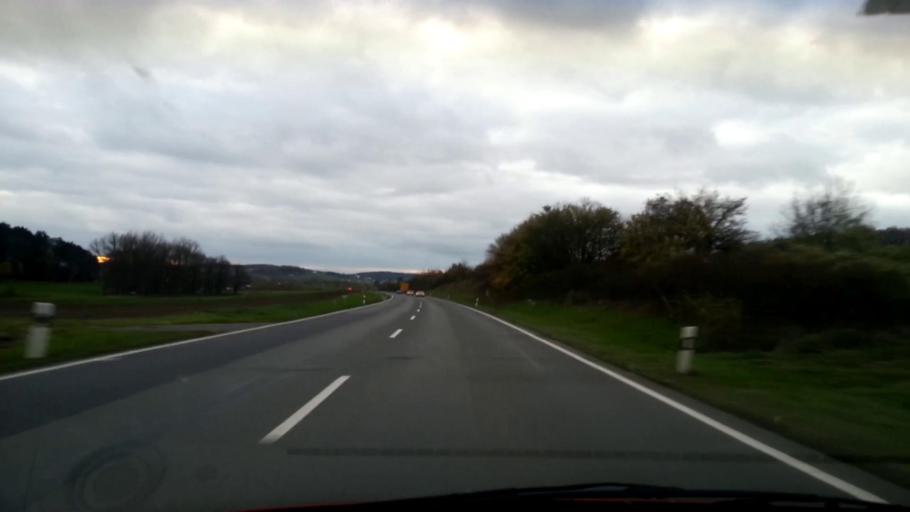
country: DE
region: Bavaria
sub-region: Upper Franconia
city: Schneckenlohe
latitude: 50.2133
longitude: 11.2372
